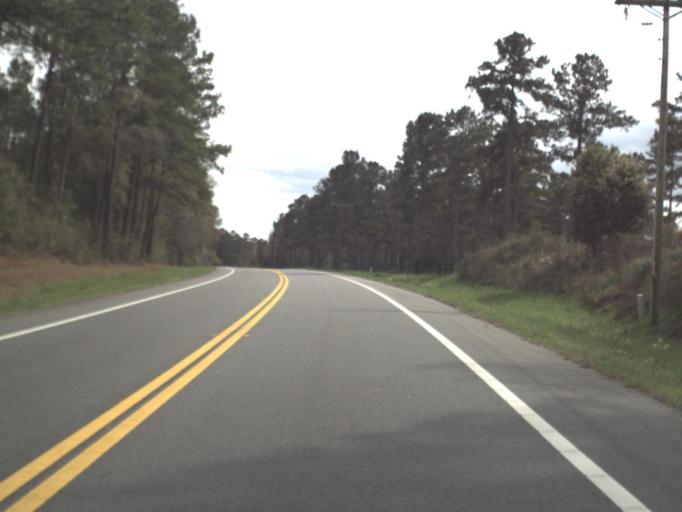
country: US
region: Florida
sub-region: Gadsden County
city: Quincy
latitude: 30.5082
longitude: -84.6097
